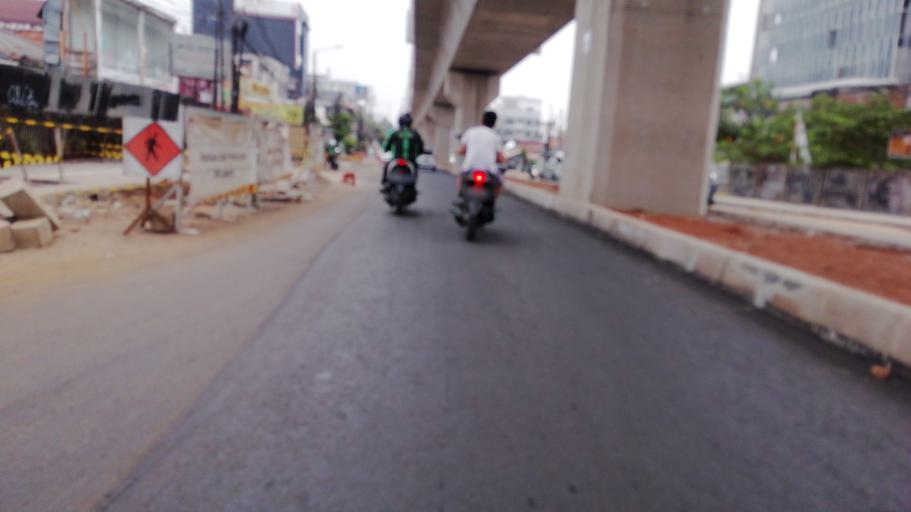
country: ID
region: Jakarta Raya
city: Jakarta
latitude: -6.2738
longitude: 106.7977
